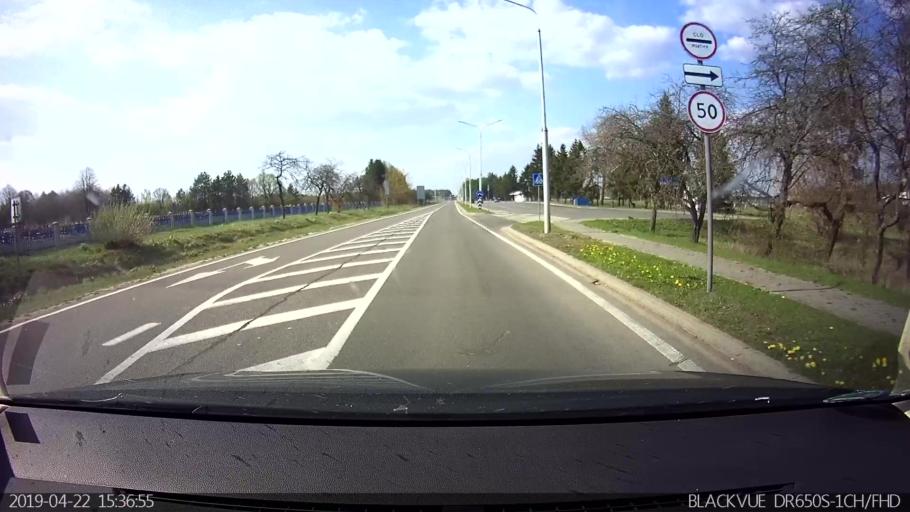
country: PL
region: Podlasie
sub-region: Powiat hajnowski
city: Czeremcha
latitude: 52.4599
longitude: 23.3646
